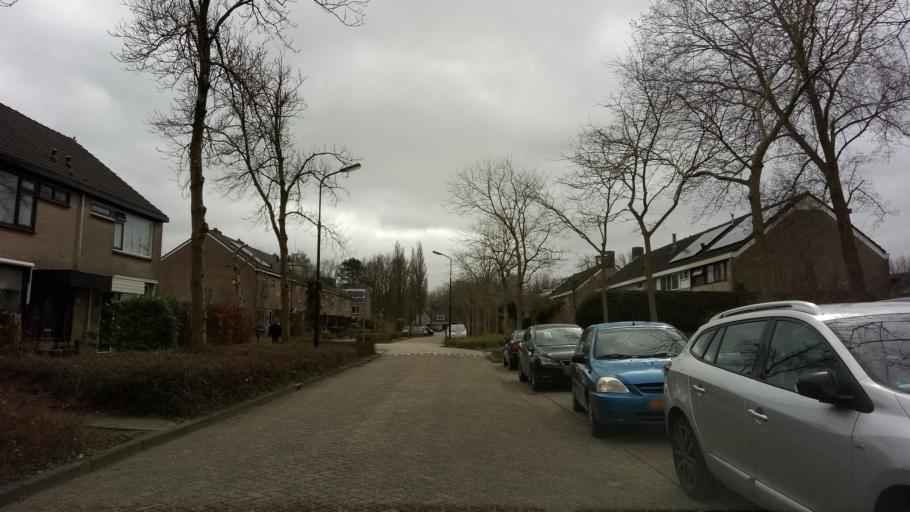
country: NL
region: North Holland
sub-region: Gemeente Heerhugowaard
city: Heerhugowaard
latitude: 52.6780
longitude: 4.8576
